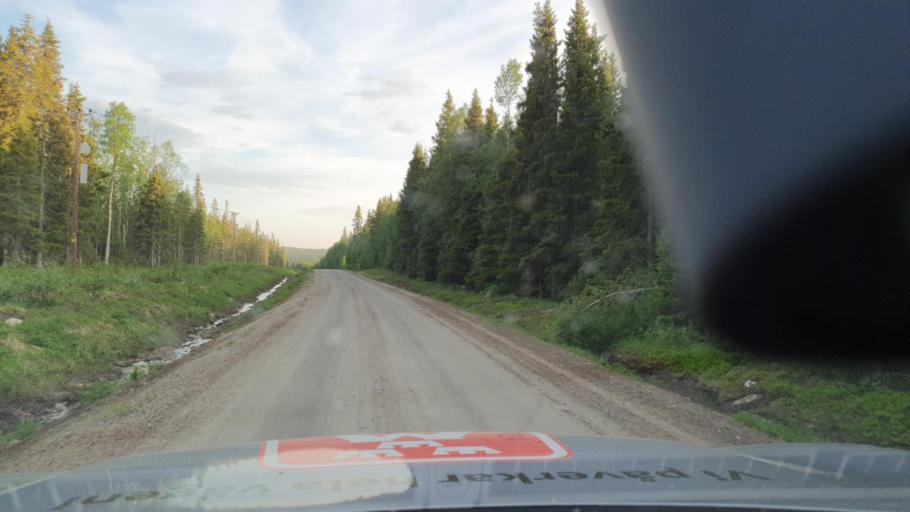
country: SE
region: Norrbotten
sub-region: Bodens Kommun
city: Boden
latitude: 66.3718
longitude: 21.5119
